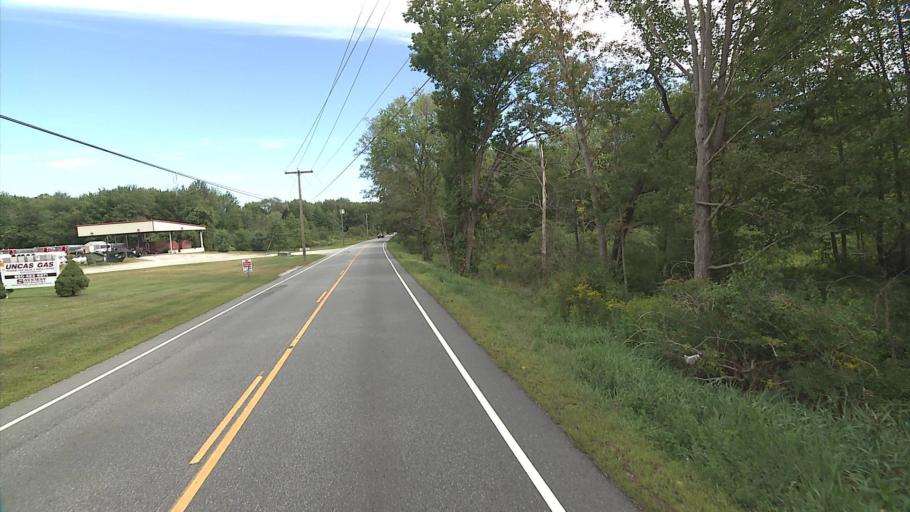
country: US
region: Connecticut
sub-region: Windham County
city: South Windham
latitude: 41.6507
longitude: -72.1597
